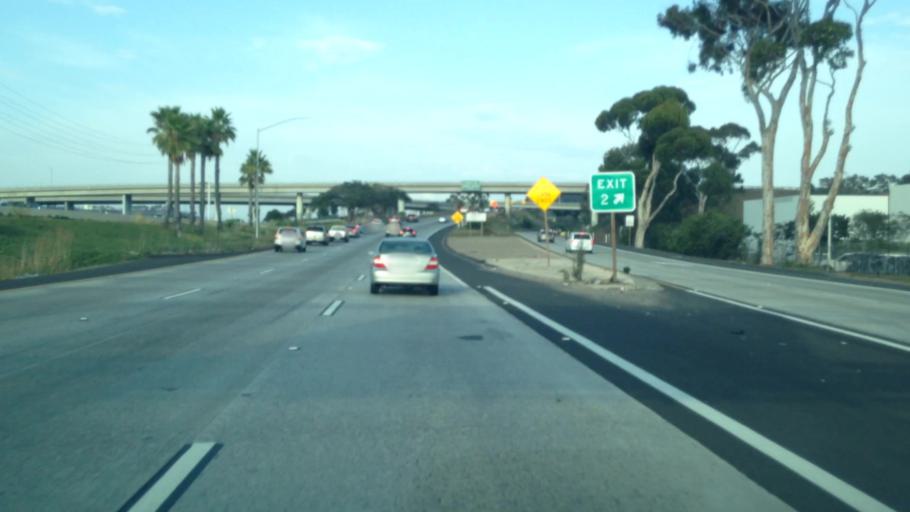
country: US
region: California
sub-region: San Diego County
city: San Diego
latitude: 32.7591
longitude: -117.2082
